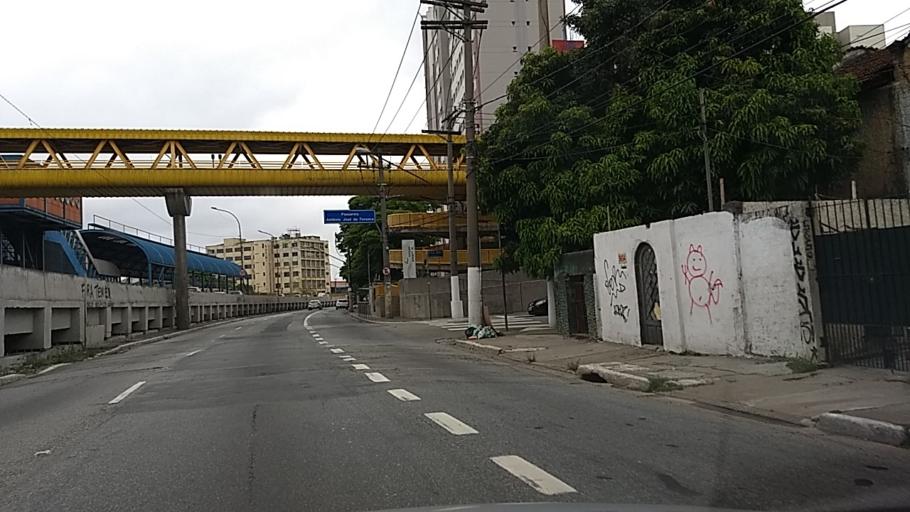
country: BR
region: Sao Paulo
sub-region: Sao Paulo
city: Sao Paulo
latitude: -23.5587
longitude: -46.6155
